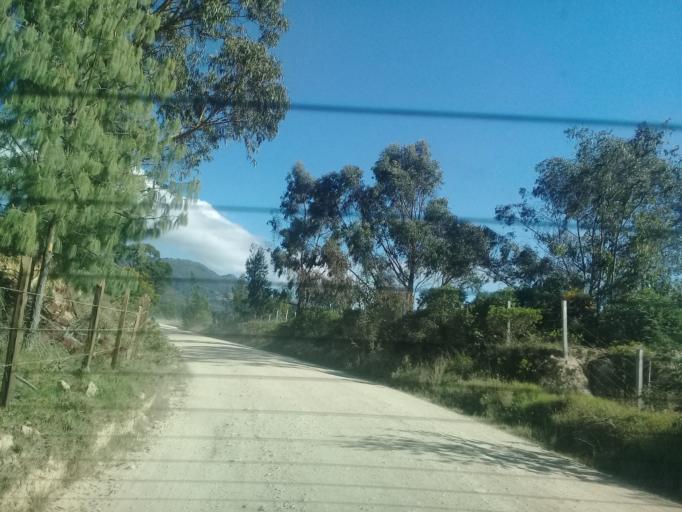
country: CO
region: Cundinamarca
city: Guasca
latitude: 4.9110
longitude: -73.8859
